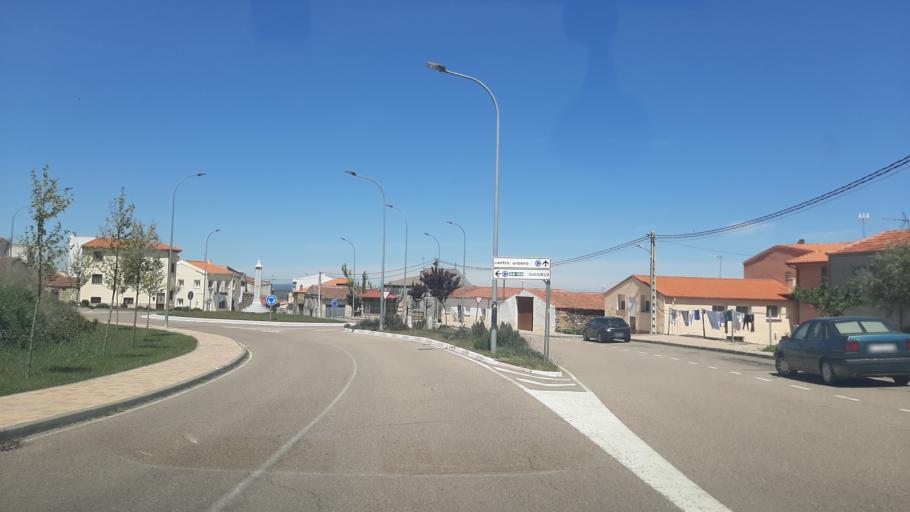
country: ES
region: Castille and Leon
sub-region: Provincia de Salamanca
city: Salvatierra de Tormes
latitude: 40.5413
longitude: -5.5780
